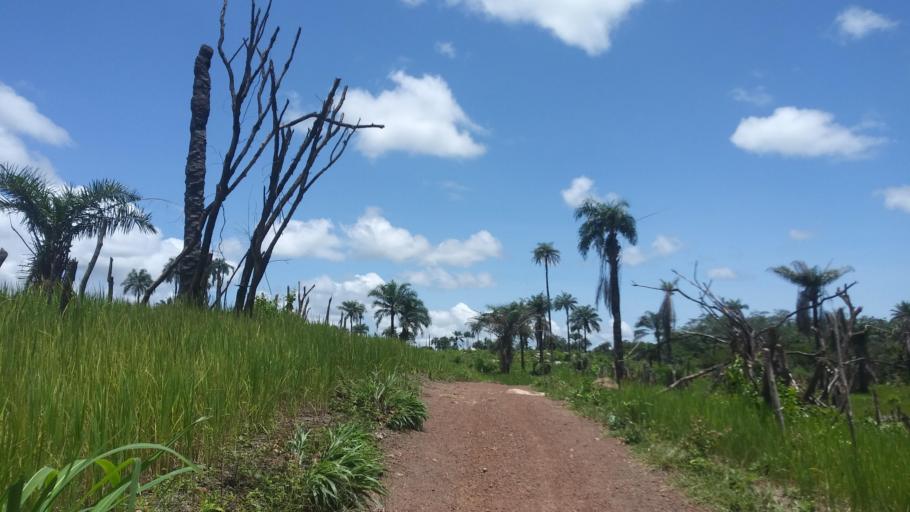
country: SL
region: Northern Province
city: Makeni
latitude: 8.8937
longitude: -12.0039
